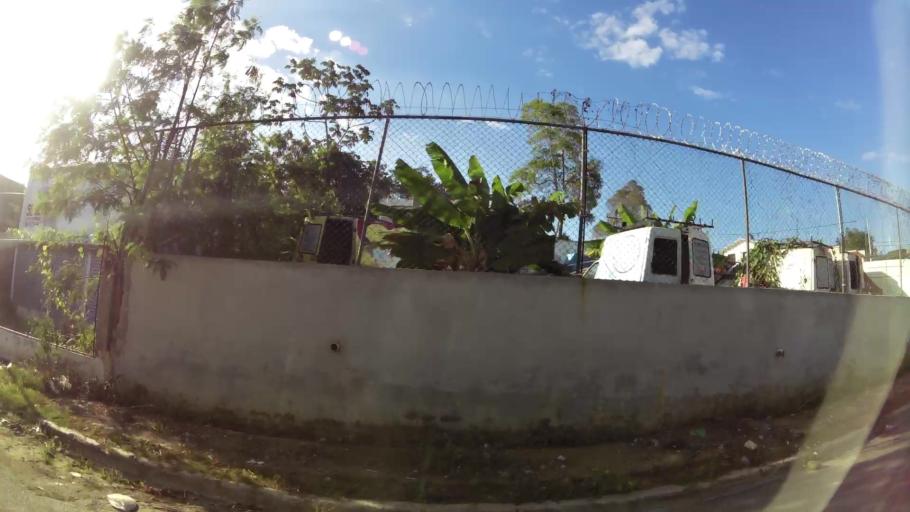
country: DO
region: Nacional
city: Ensanche Luperon
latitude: 18.5464
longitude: -69.9125
